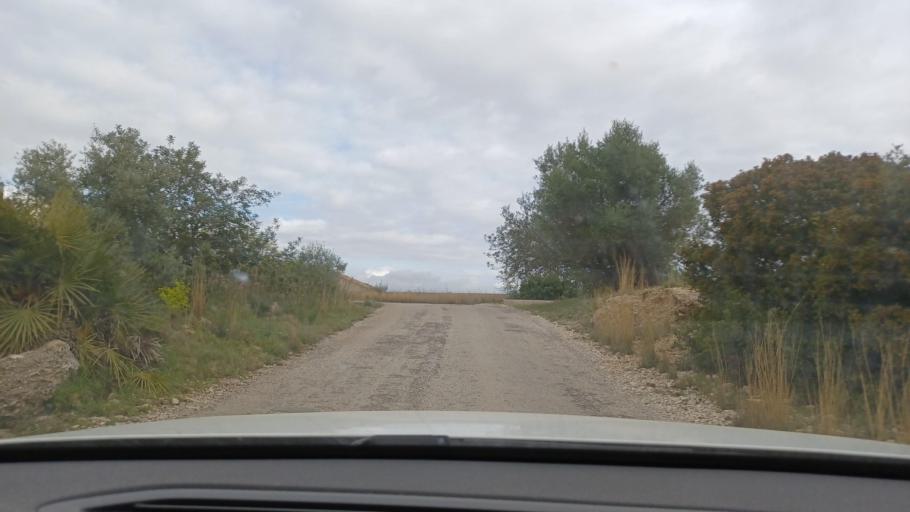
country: ES
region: Catalonia
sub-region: Provincia de Tarragona
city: Tortosa
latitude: 40.7916
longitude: 0.4673
